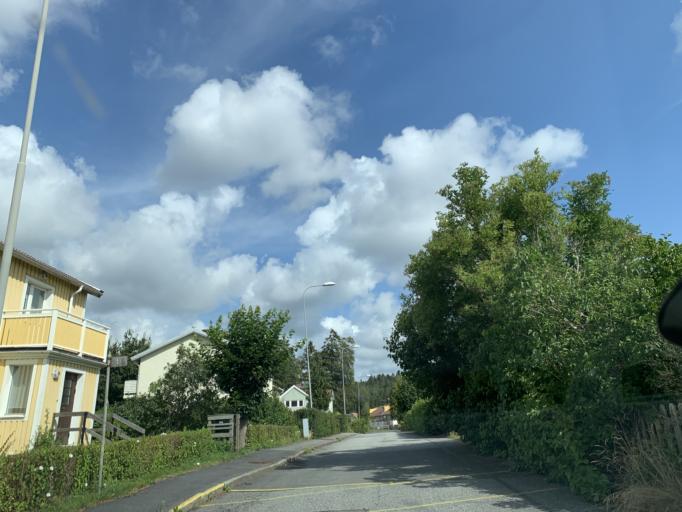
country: SE
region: Vaestra Goetaland
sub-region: Goteborg
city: Eriksbo
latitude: 57.7431
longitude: 12.0488
